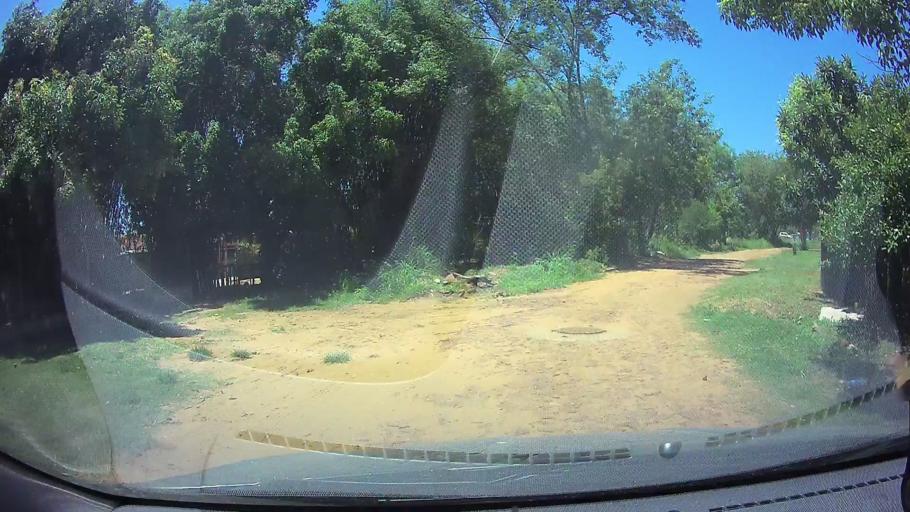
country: PY
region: Central
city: San Lorenzo
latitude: -25.3478
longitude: -57.4901
